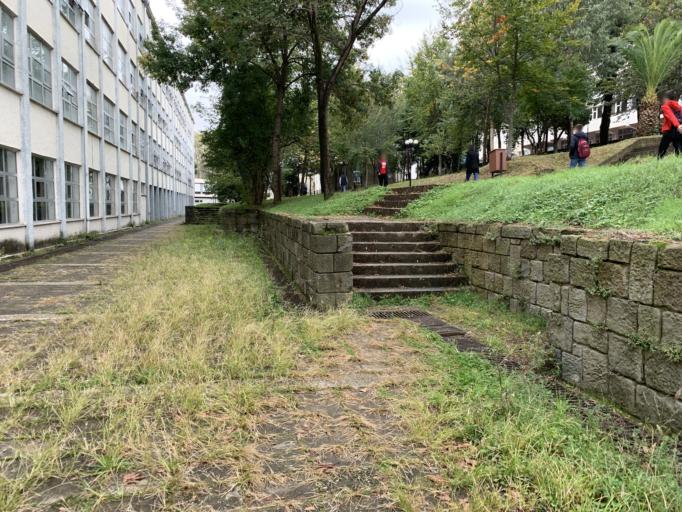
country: TR
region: Trabzon
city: Trabzon
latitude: 40.9956
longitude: 39.7722
